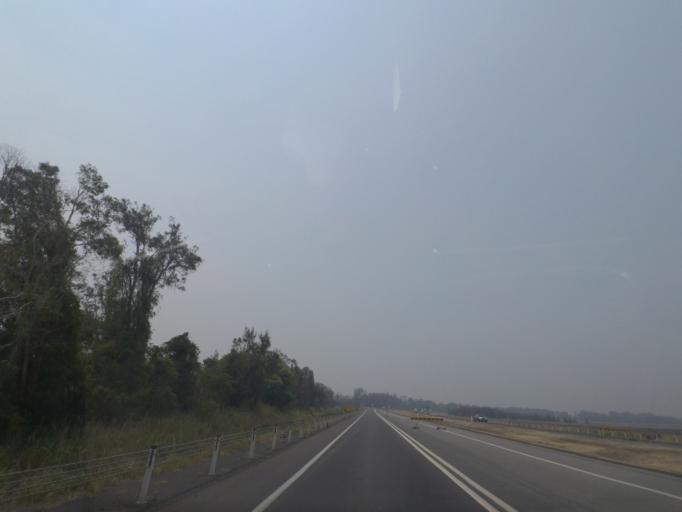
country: AU
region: New South Wales
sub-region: Ballina
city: Ballina
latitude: -28.8725
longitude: 153.4902
